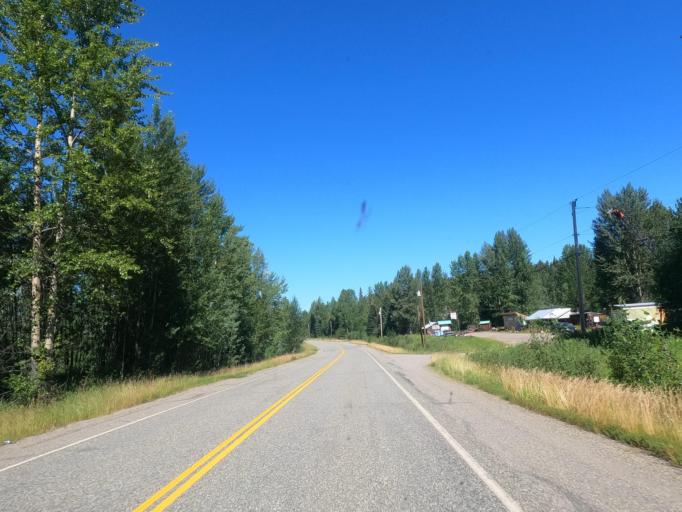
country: CA
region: British Columbia
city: Quesnel
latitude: 53.0410
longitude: -122.1385
